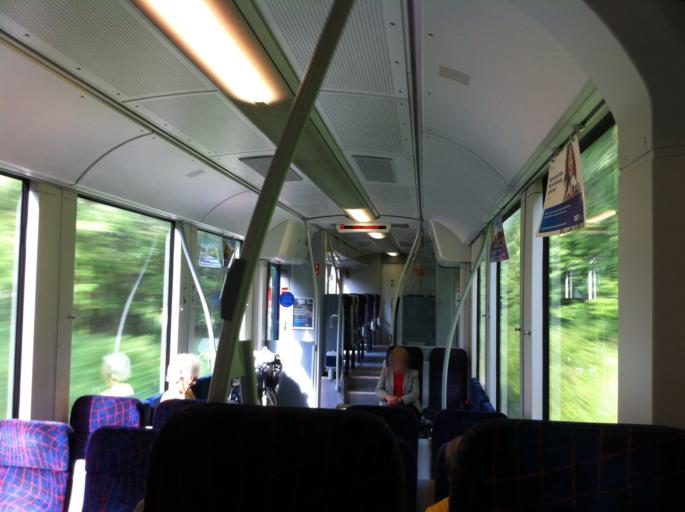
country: DK
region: Capital Region
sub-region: Gribskov Kommune
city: Gilleleje
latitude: 56.0982
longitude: 12.3447
